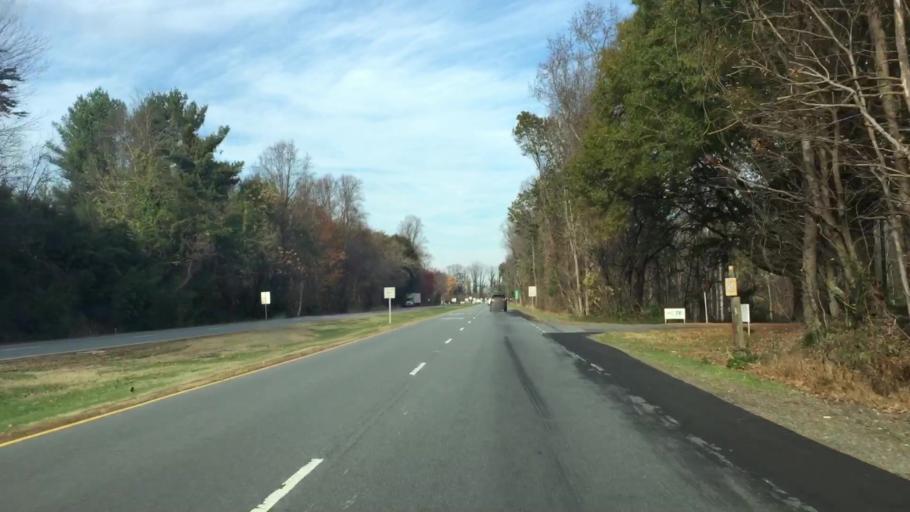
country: US
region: North Carolina
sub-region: Forsyth County
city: Winston-Salem
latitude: 36.1107
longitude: -80.1892
